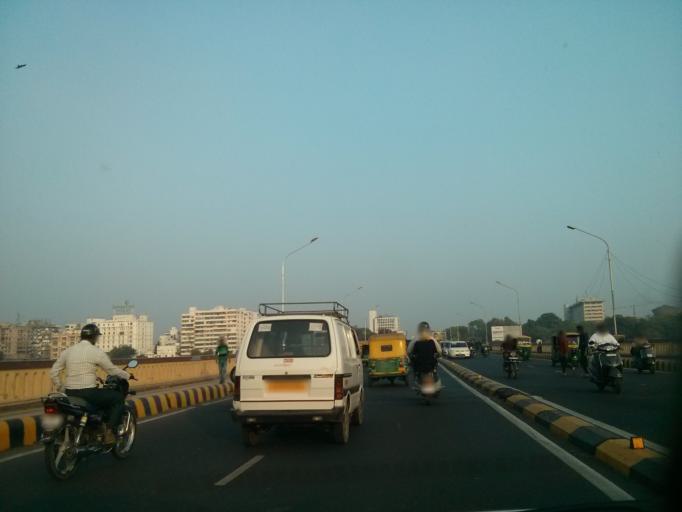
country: IN
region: Gujarat
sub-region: Ahmadabad
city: Ahmedabad
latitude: 23.0269
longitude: 72.5731
